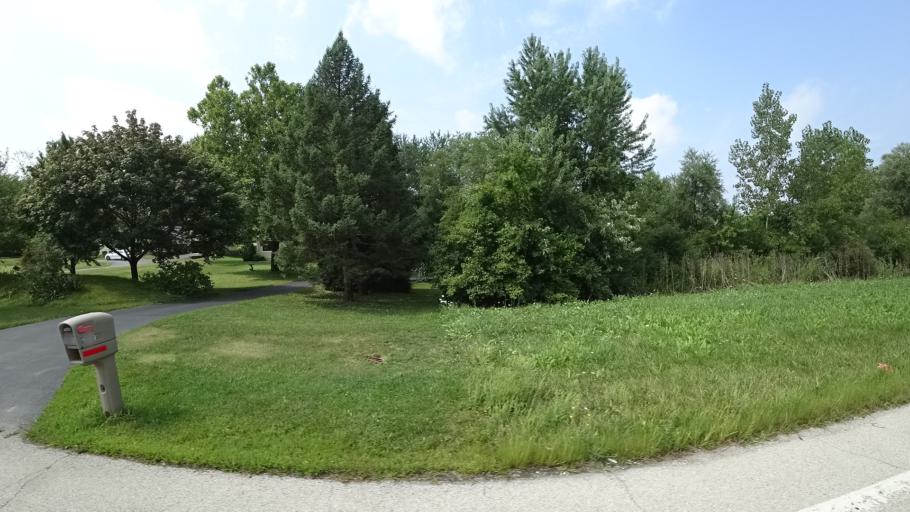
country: US
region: Illinois
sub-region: Cook County
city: Orland Park
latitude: 41.6278
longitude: -87.8827
